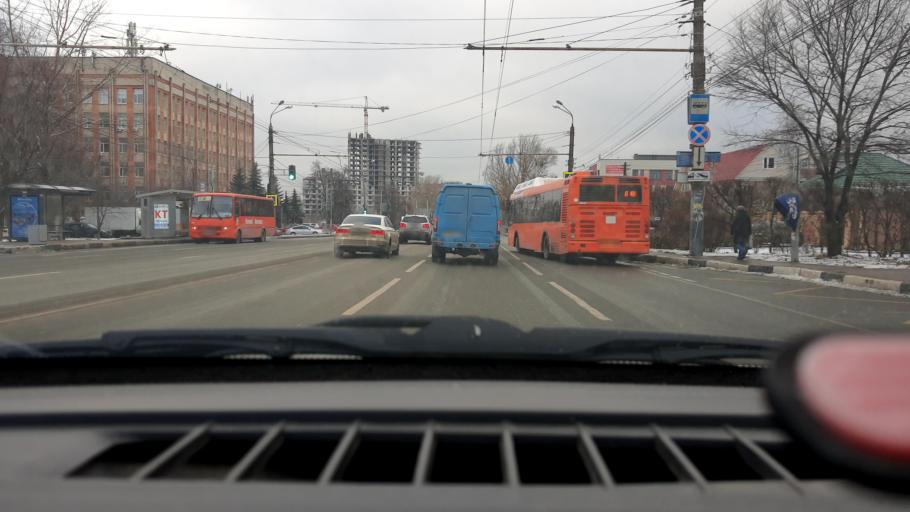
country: RU
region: Nizjnij Novgorod
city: Bor
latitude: 56.3184
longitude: 44.0643
